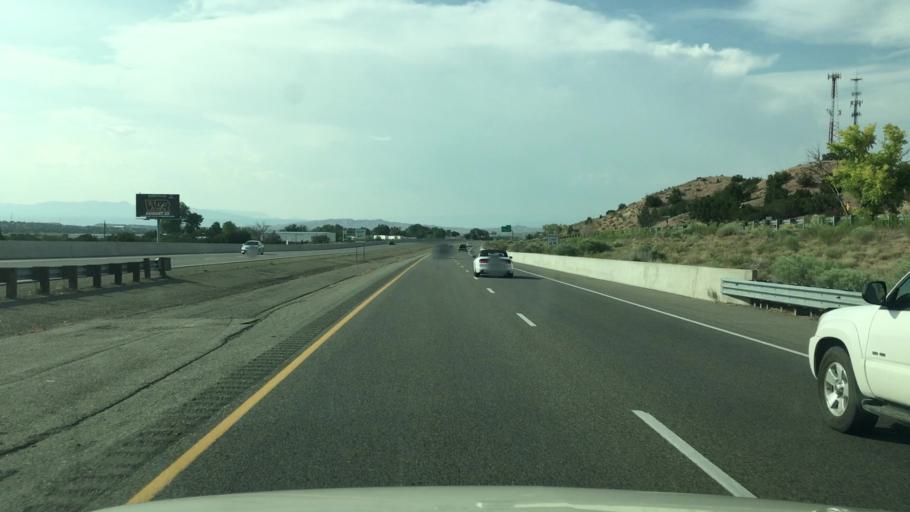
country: US
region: New Mexico
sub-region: Santa Fe County
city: Nambe
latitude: 35.8444
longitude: -105.9923
